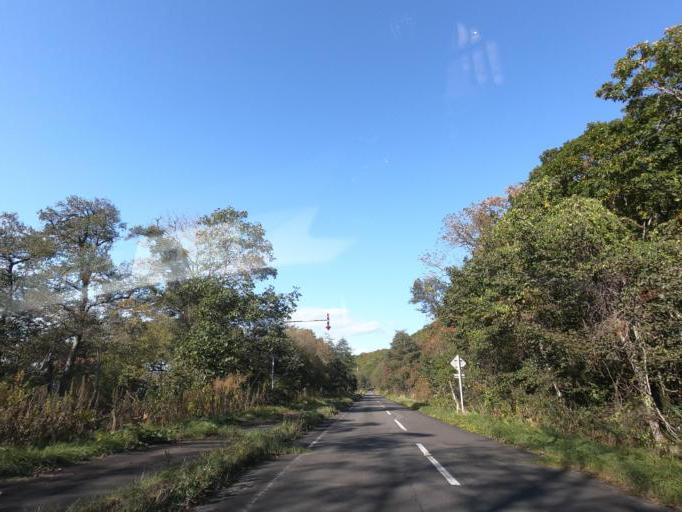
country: JP
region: Hokkaido
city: Obihiro
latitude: 42.6110
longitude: 143.5446
